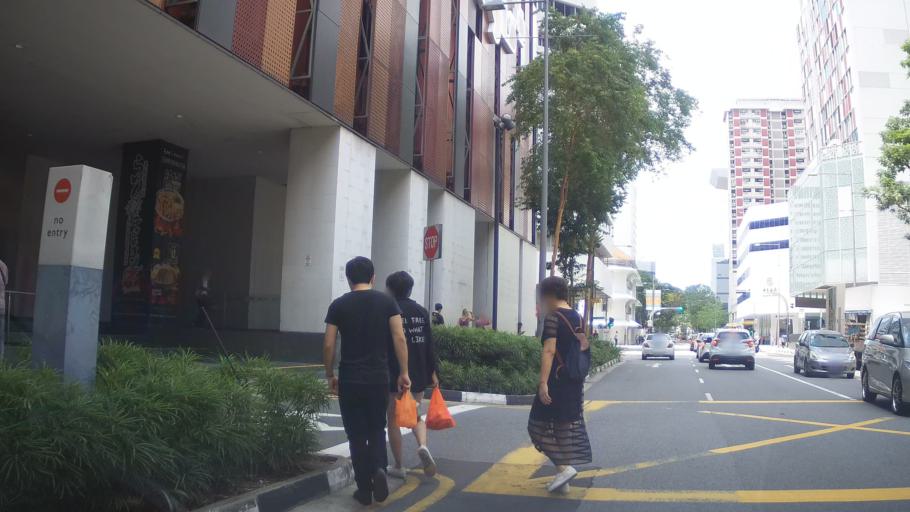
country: SG
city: Singapore
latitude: 1.3000
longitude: 103.8539
